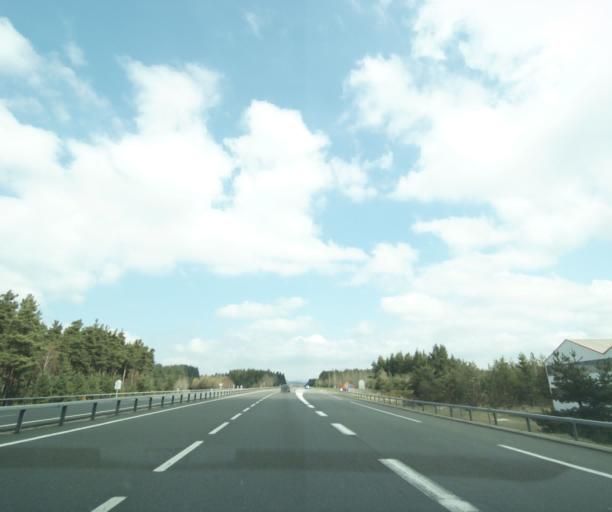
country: FR
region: Languedoc-Roussillon
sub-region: Departement de la Lozere
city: Aumont-Aubrac
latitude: 44.7740
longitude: 3.2858
